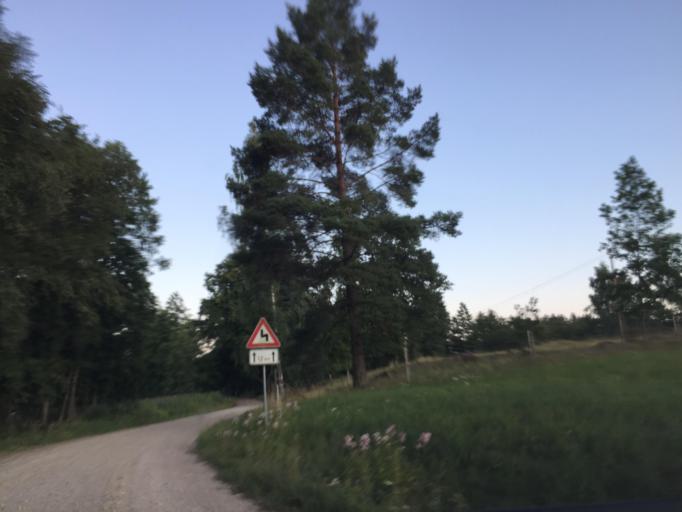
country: LV
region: Talsu Rajons
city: Stende
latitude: 57.1549
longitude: 22.2949
